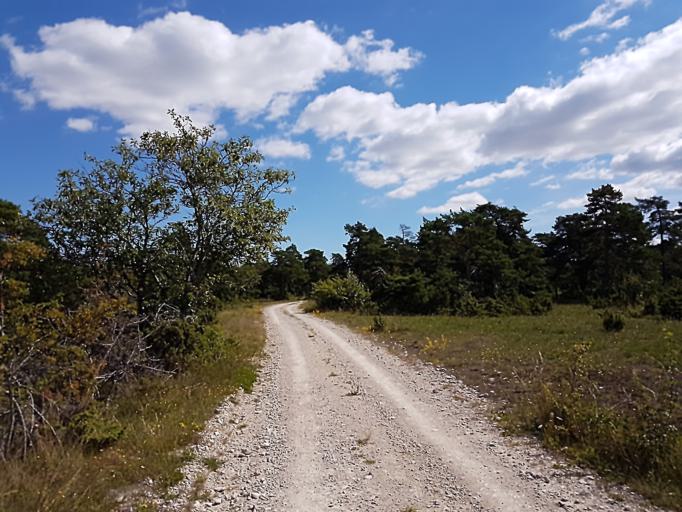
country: SE
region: Gotland
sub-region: Gotland
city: Visby
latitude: 57.6105
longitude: 18.3275
